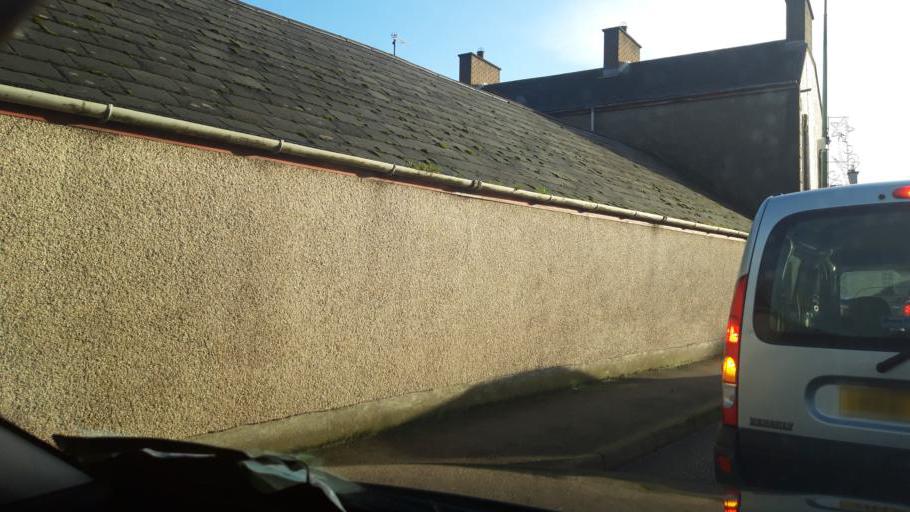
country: GB
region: Northern Ireland
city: Maghera
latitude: 54.8120
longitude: -6.7060
